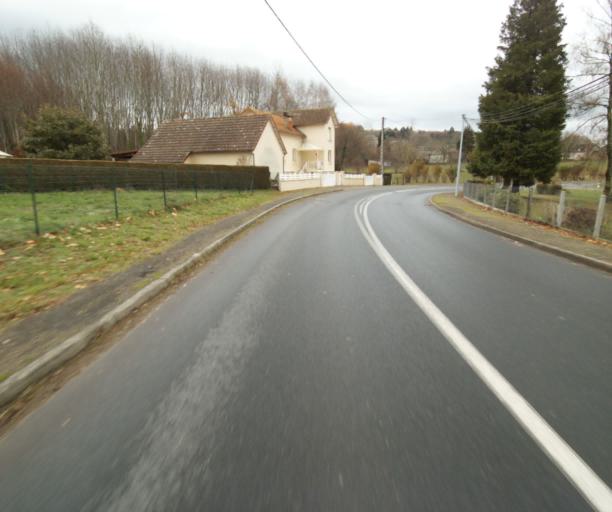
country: FR
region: Limousin
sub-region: Departement de la Correze
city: Saint-Mexant
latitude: 45.2757
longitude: 1.6314
